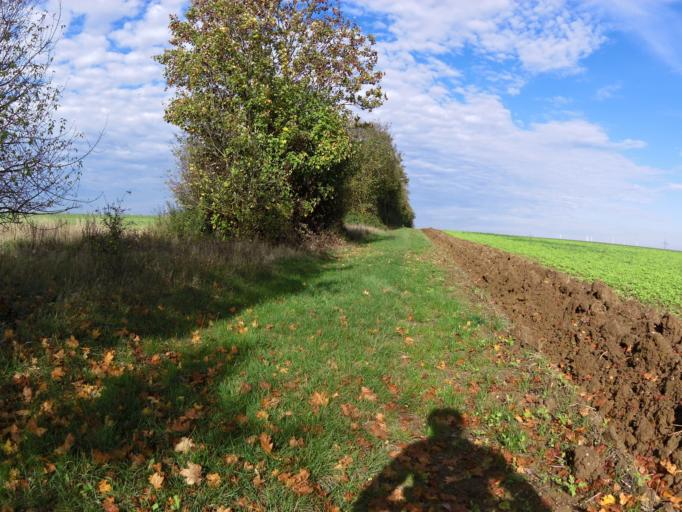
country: DE
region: Bavaria
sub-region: Regierungsbezirk Unterfranken
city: Frickenhausen
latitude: 49.7149
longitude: 10.0734
